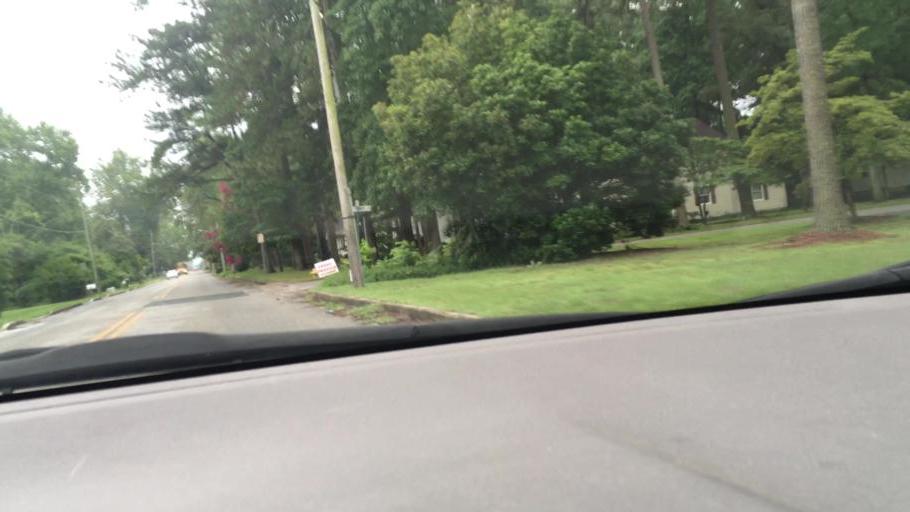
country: US
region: Maryland
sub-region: Wicomico County
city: Fruitland
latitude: 38.3315
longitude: -75.6262
